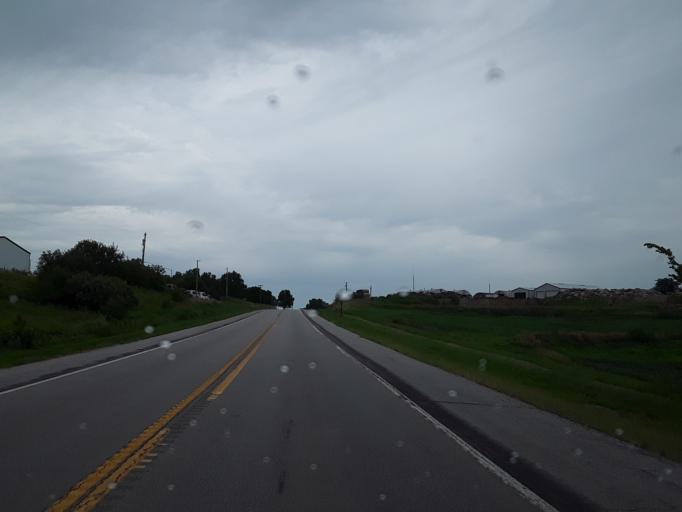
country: US
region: Nebraska
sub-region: Washington County
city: Blair
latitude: 41.5043
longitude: -96.1592
